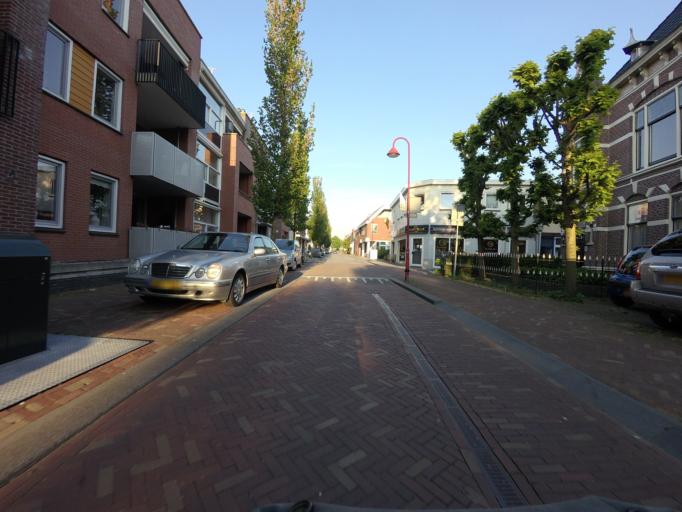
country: NL
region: South Holland
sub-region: Bodegraven-Reeuwijk
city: Bodegraven
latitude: 52.0839
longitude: 4.7491
